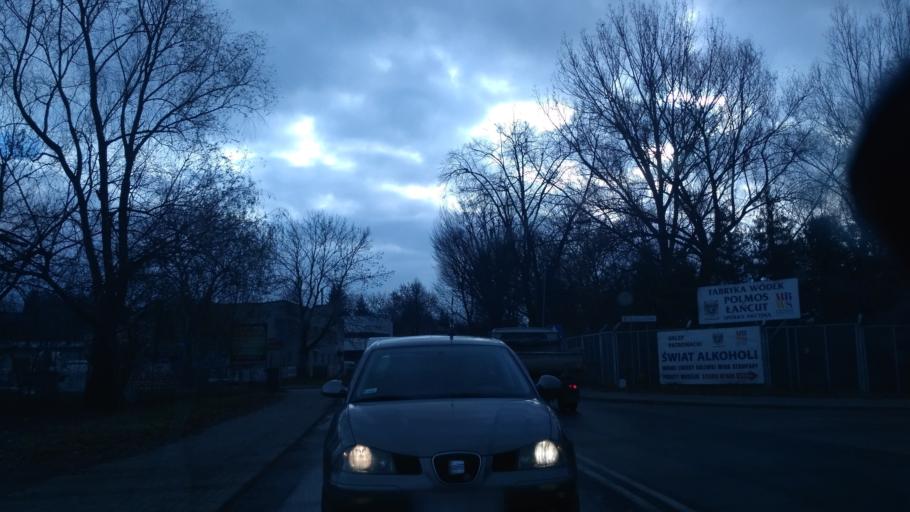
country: PL
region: Subcarpathian Voivodeship
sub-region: Powiat lancucki
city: Lancut
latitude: 50.0815
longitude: 22.2329
